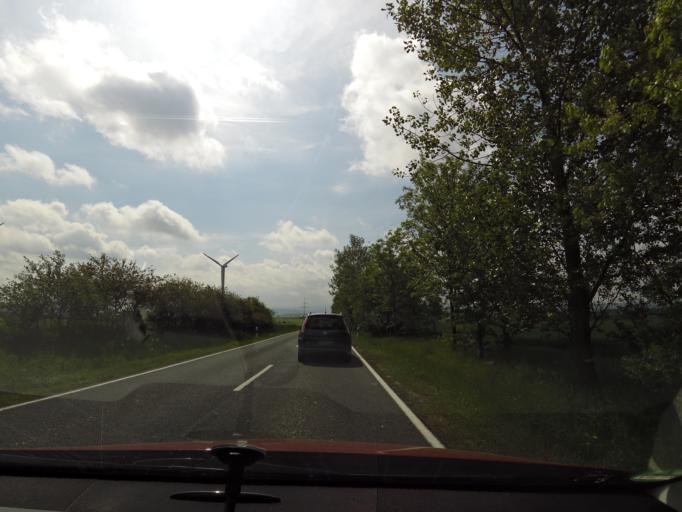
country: DE
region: Thuringia
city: Lauterbach
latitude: 51.0366
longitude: 10.3300
